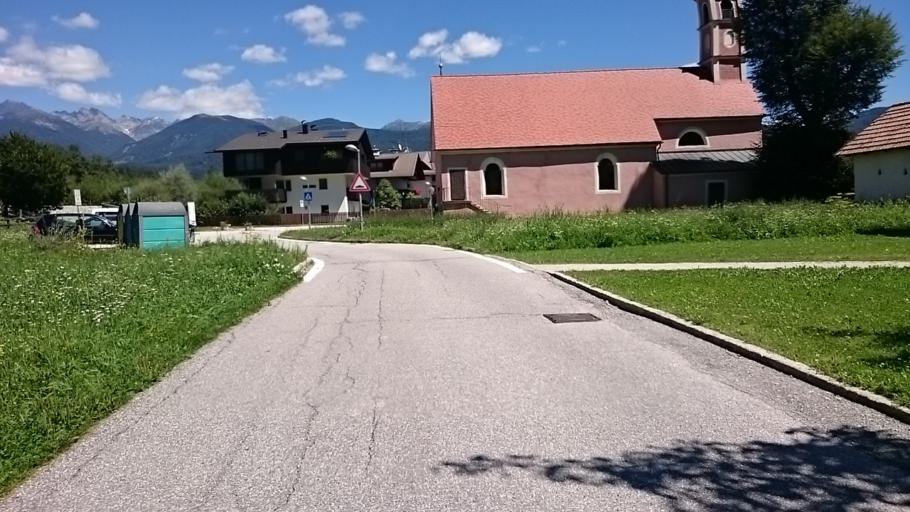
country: IT
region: Trentino-Alto Adige
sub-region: Bolzano
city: San Lorenzo di Sebato
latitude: 46.7864
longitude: 11.9096
